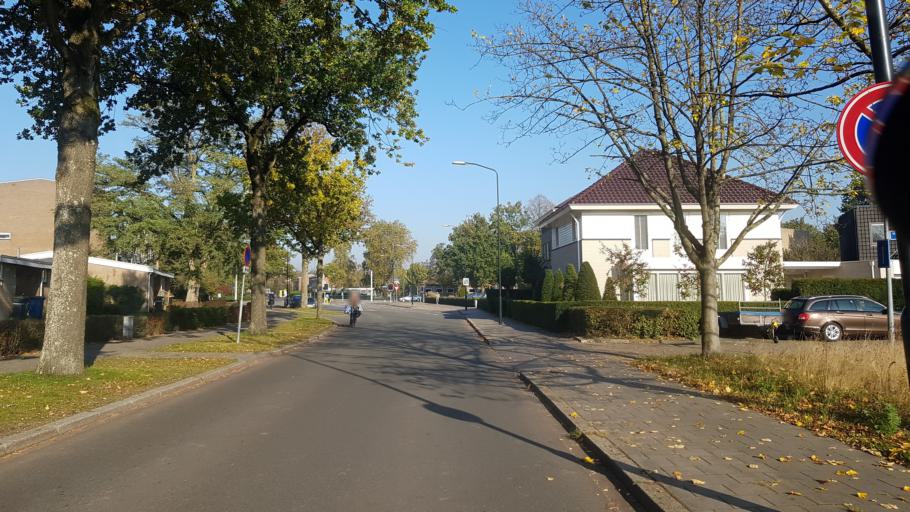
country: NL
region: Gelderland
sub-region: Gemeente Apeldoorn
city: Apeldoorn
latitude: 52.2299
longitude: 5.9683
